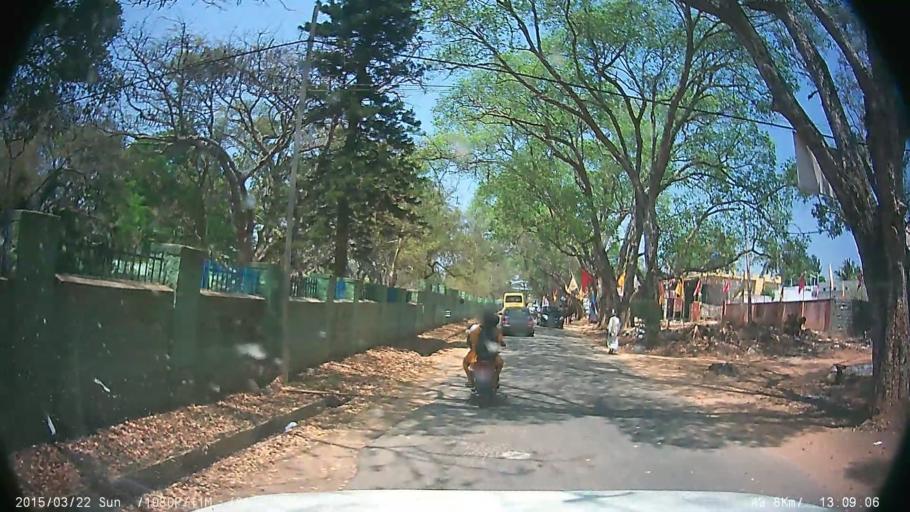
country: IN
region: Karnataka
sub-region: Bangalore Urban
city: Anekal
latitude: 12.8015
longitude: 77.5769
